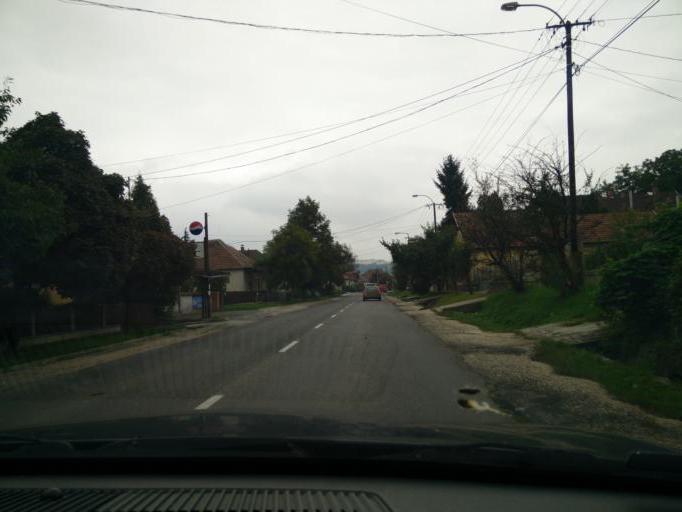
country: HU
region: Komarom-Esztergom
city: Kesztolc
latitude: 47.6802
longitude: 18.7764
